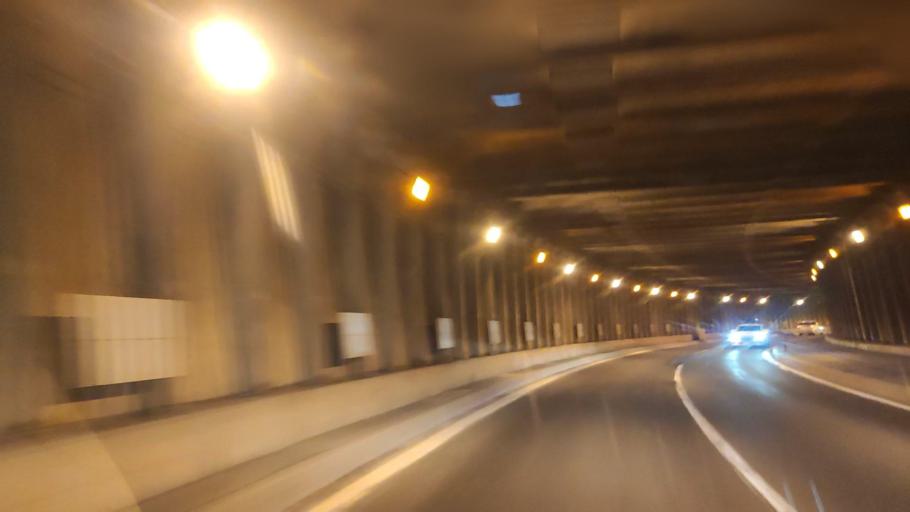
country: JP
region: Hokkaido
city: Ishikari
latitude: 43.3337
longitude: 141.4415
